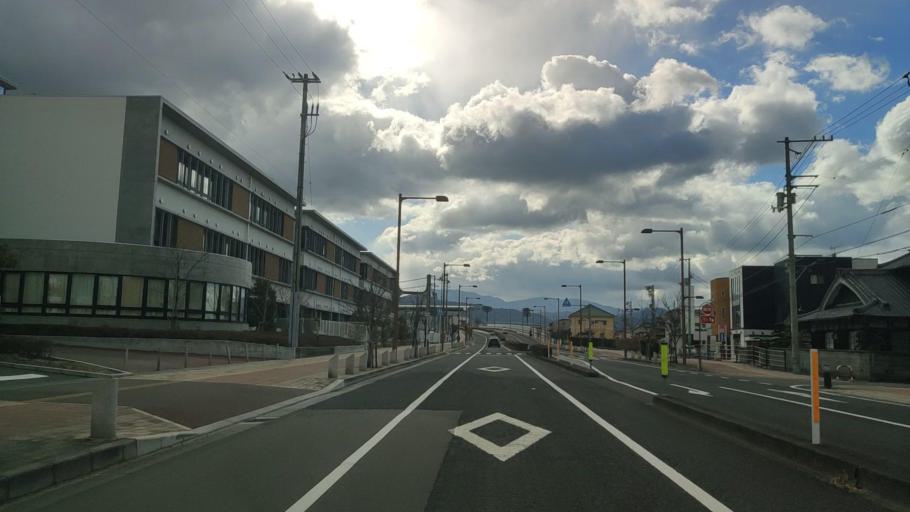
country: JP
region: Ehime
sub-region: Shikoku-chuo Shi
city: Matsuyama
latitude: 33.8140
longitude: 132.7408
